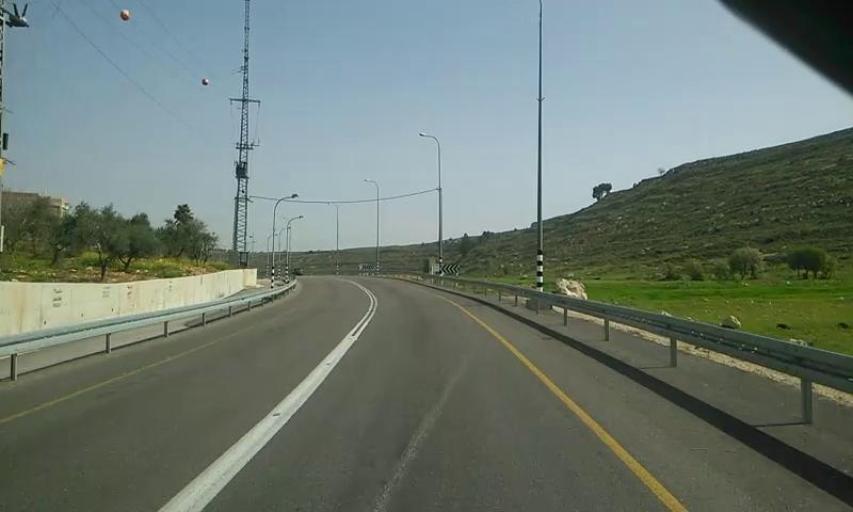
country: PS
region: West Bank
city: Sinjil
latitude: 32.0277
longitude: 35.2732
